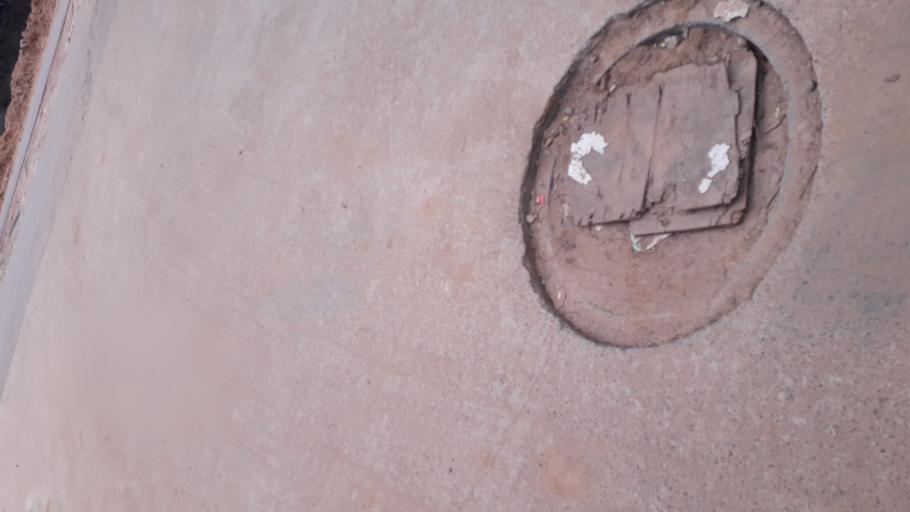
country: IN
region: Telangana
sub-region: Rangareddi
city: Kukatpalli
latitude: 17.4505
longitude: 78.3581
